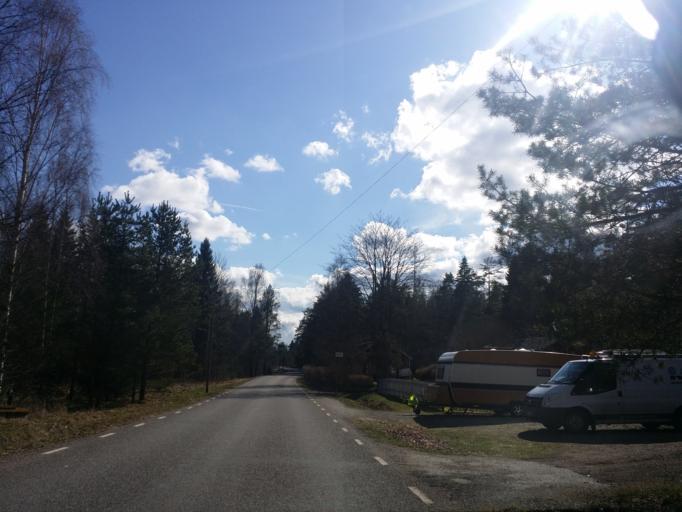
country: SE
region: Vaestmanland
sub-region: Sala Kommun
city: Sala
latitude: 59.9961
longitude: 16.4869
